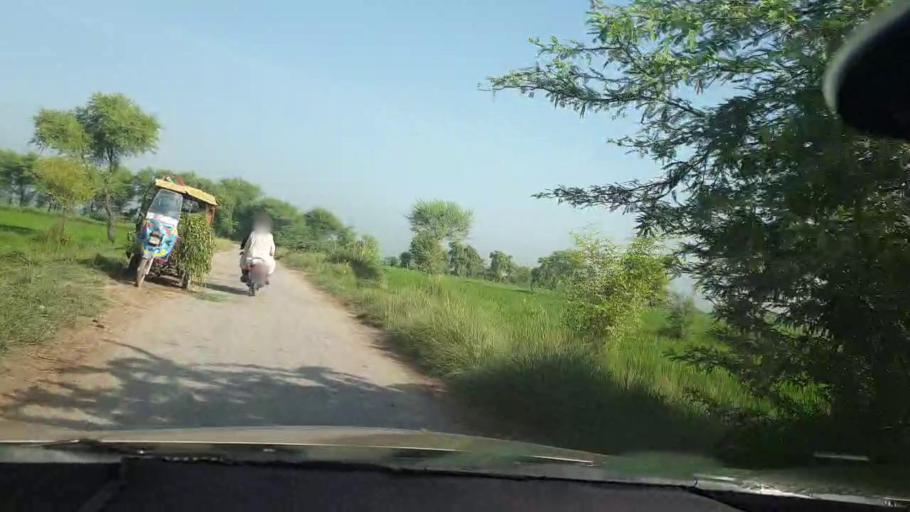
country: PK
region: Sindh
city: Kambar
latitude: 27.6599
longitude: 68.0226
